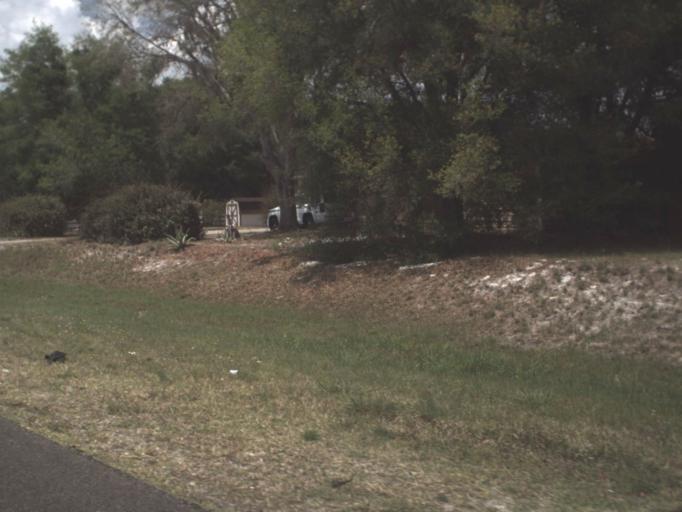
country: US
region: Florida
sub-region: Citrus County
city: Inverness
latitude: 28.8546
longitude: -82.2039
